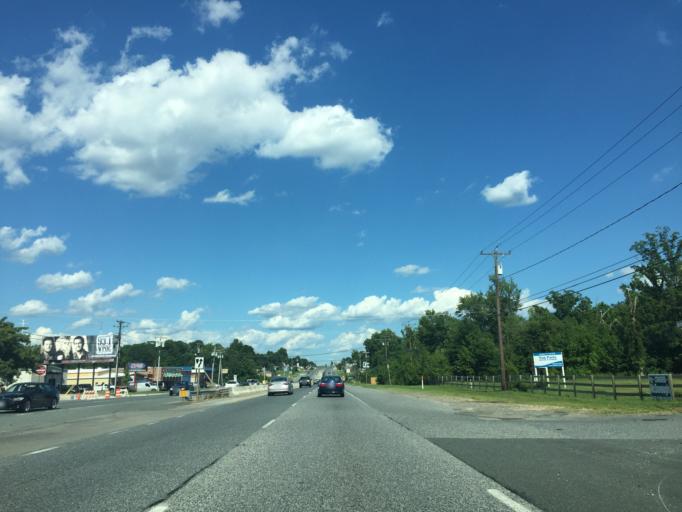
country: US
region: Maryland
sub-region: Harford County
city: Joppatowne
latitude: 39.4295
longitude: -76.3524
